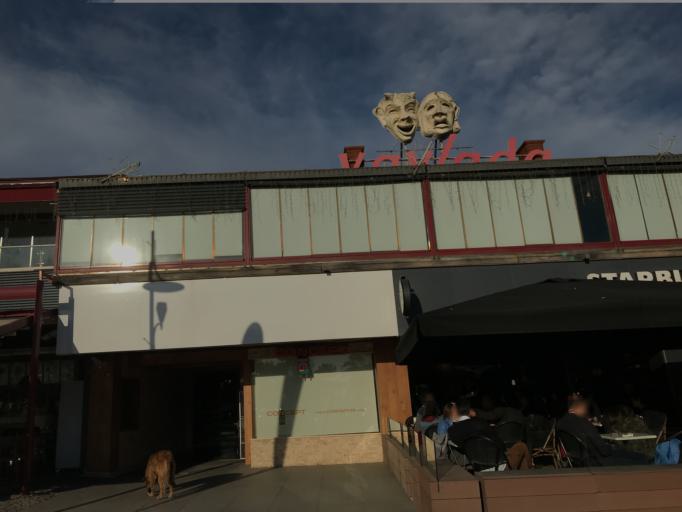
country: TR
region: Istanbul
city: Maltepe
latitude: 40.9268
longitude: 29.1234
